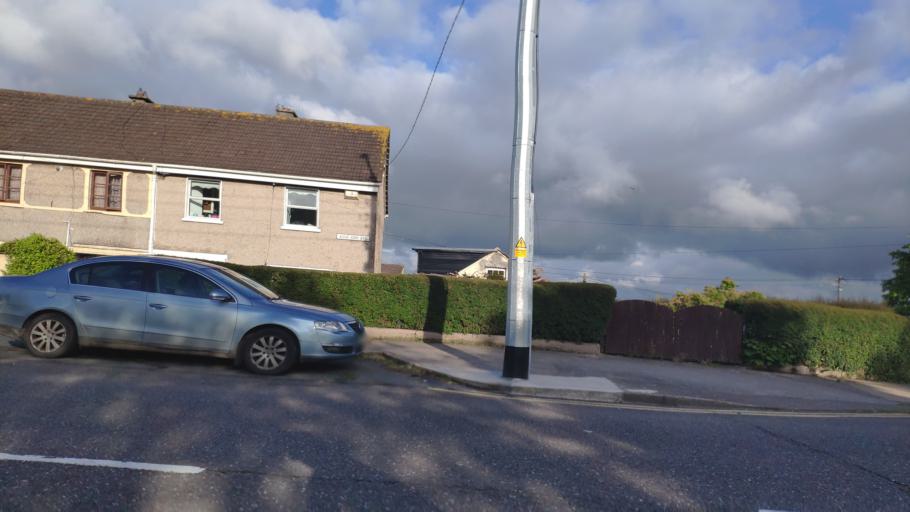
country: IE
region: Munster
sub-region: County Cork
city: Cork
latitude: 51.9114
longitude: -8.4837
